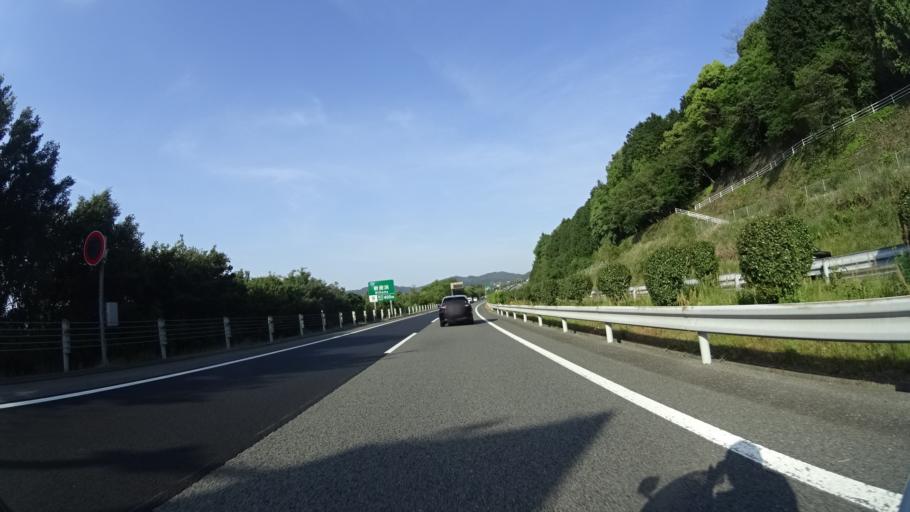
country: JP
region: Ehime
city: Niihama
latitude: 33.9238
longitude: 133.3192
